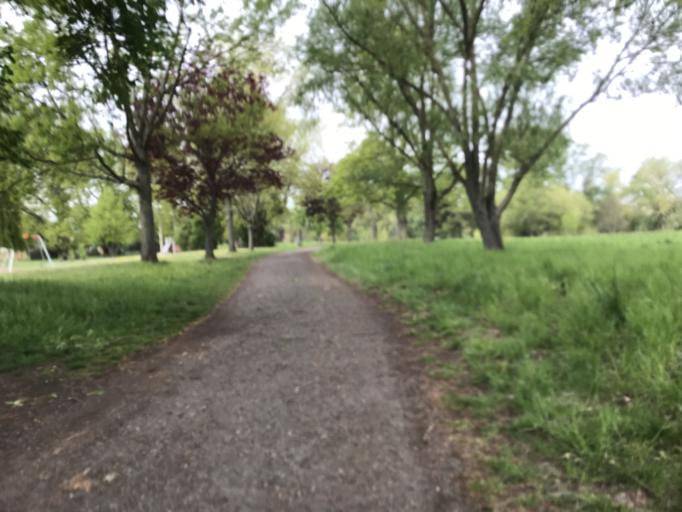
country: DE
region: Rheinland-Pfalz
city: Mainz
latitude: 50.0000
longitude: 8.3146
